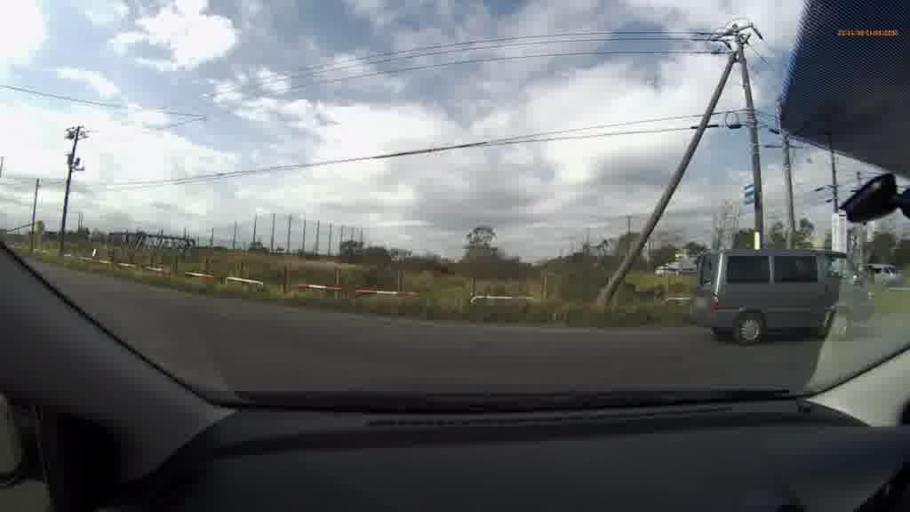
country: JP
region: Hokkaido
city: Kushiro
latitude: 43.0100
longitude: 144.2875
